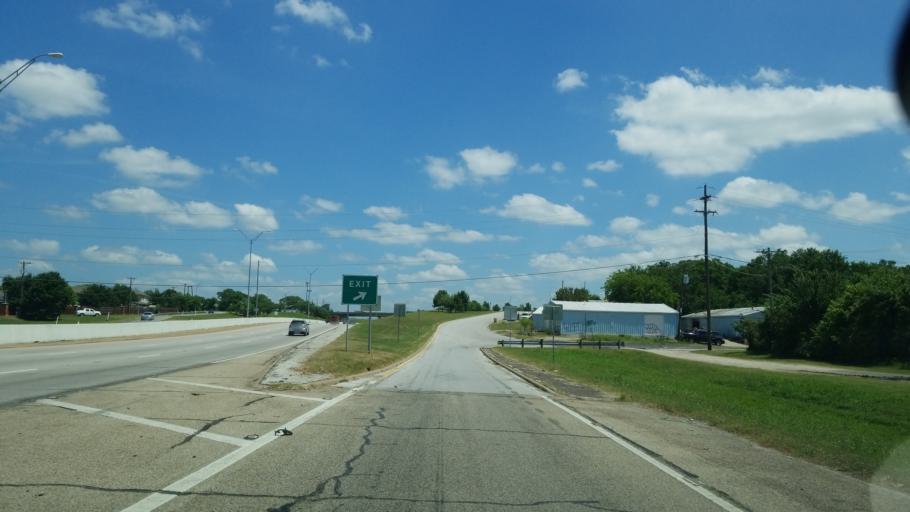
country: US
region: Texas
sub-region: Dallas County
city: Hutchins
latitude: 32.7363
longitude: -96.7158
